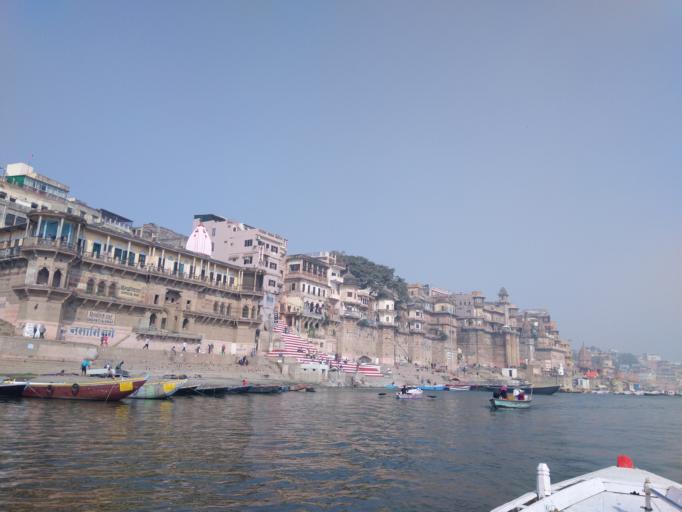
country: IN
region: Uttar Pradesh
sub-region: Varanasi
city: Varanasi
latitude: 25.3037
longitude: 83.0092
